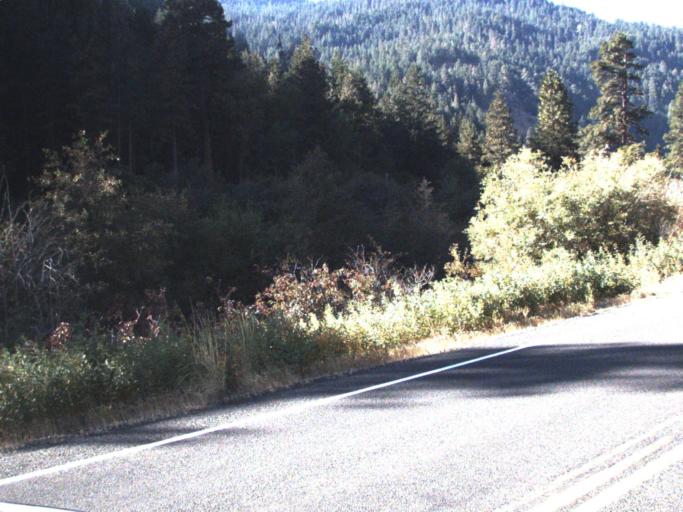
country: US
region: Washington
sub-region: Yakima County
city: Tieton
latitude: 46.6876
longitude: -120.9325
